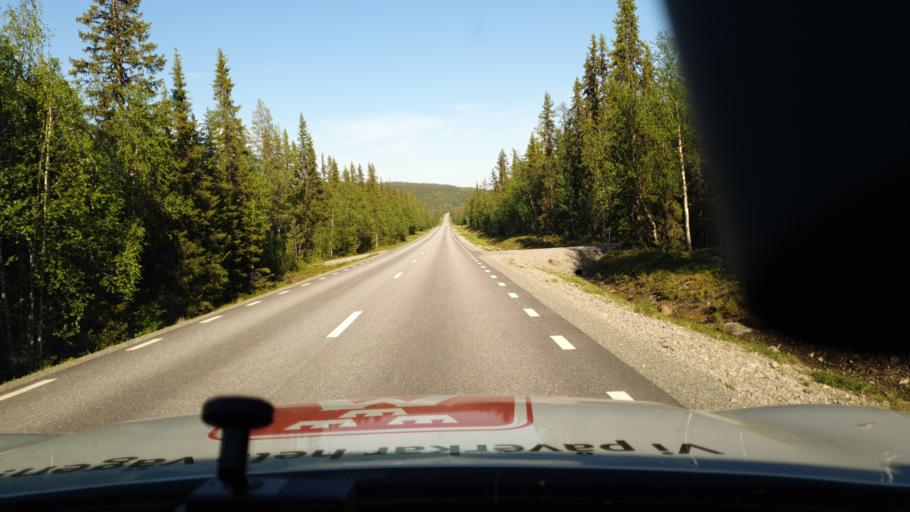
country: SE
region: Vaesterbotten
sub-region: Asele Kommun
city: Insjon
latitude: 64.7229
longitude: 17.6225
